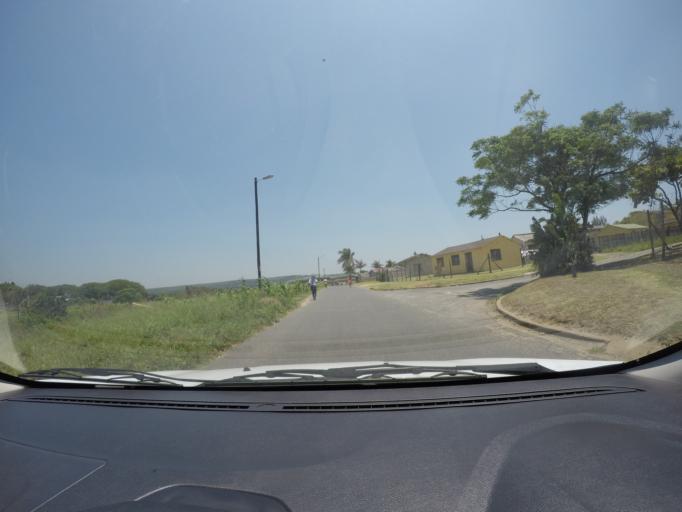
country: ZA
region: KwaZulu-Natal
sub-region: uThungulu District Municipality
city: eSikhawini
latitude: -28.8795
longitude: 31.9056
